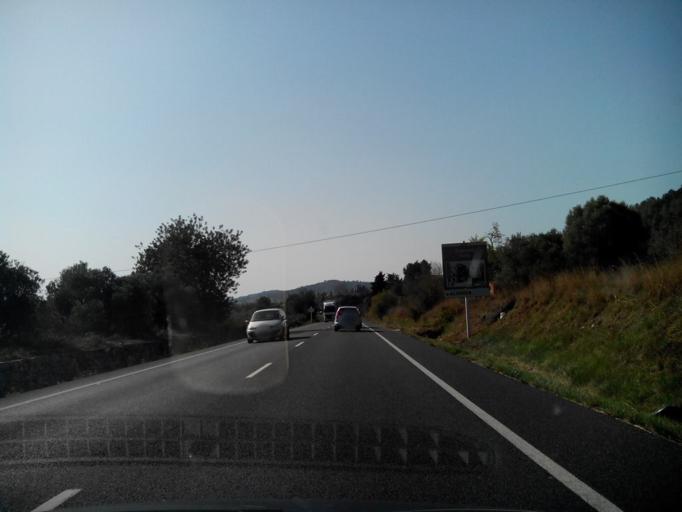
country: ES
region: Catalonia
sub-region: Provincia de Tarragona
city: Alcover
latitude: 41.2724
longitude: 1.1770
